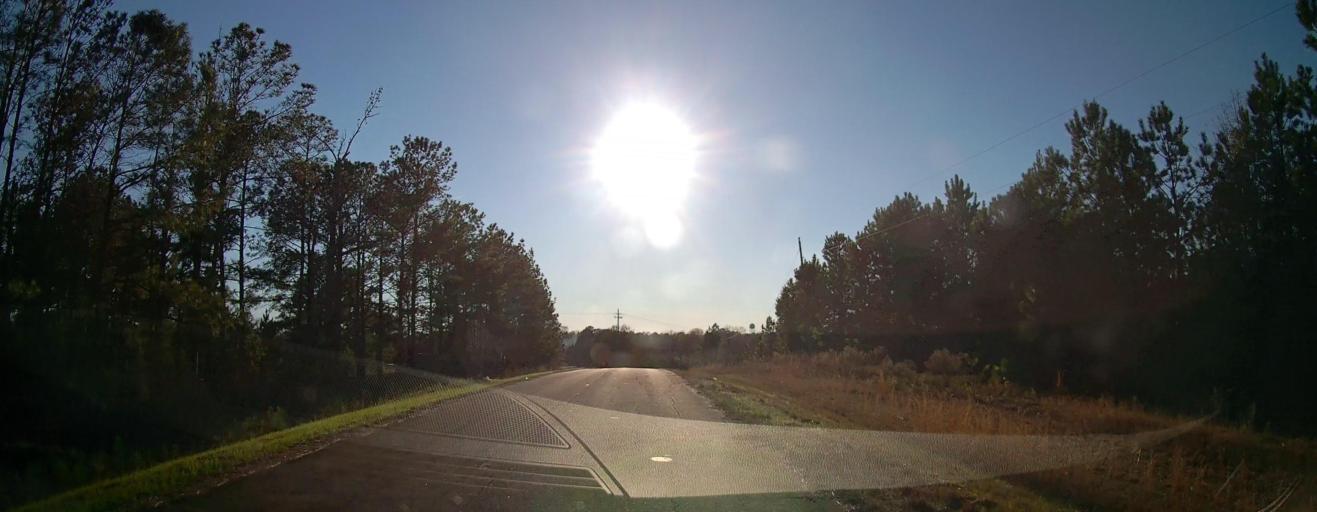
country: US
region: Georgia
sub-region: Talbot County
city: Talbotton
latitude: 32.5777
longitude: -84.5330
